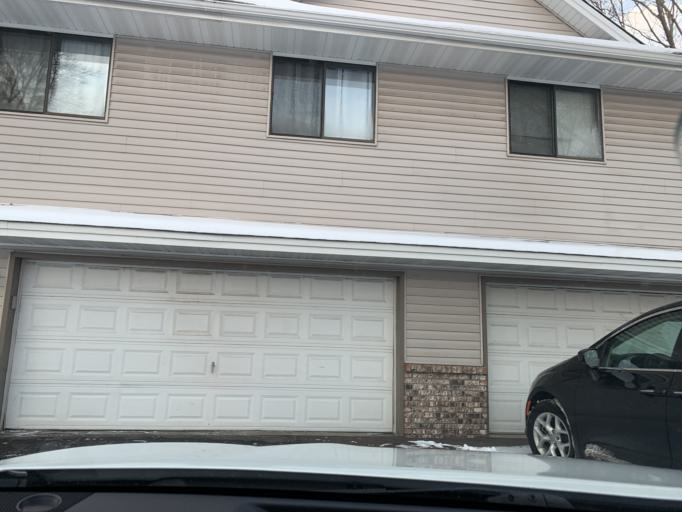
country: US
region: Minnesota
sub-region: Anoka County
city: Coon Rapids
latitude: 45.1603
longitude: -93.2896
